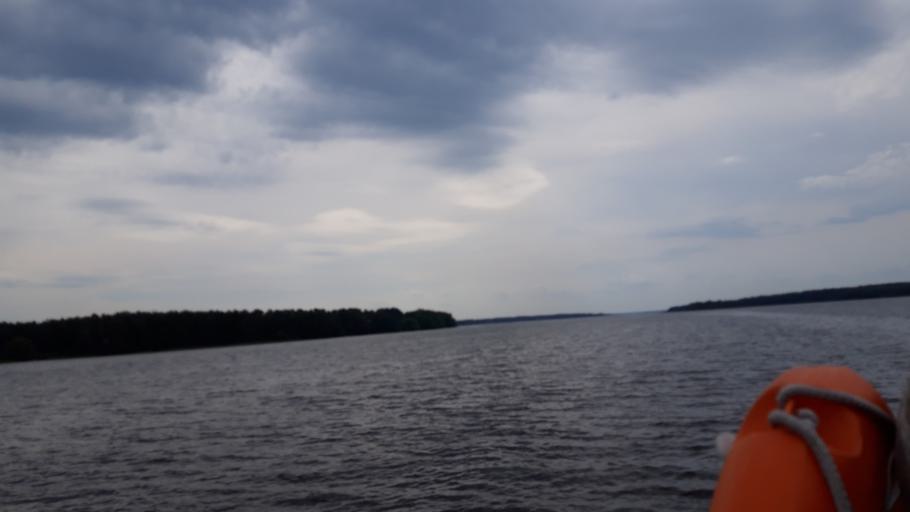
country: RU
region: Tverskaya
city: Konakovo
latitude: 56.6977
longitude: 36.7051
